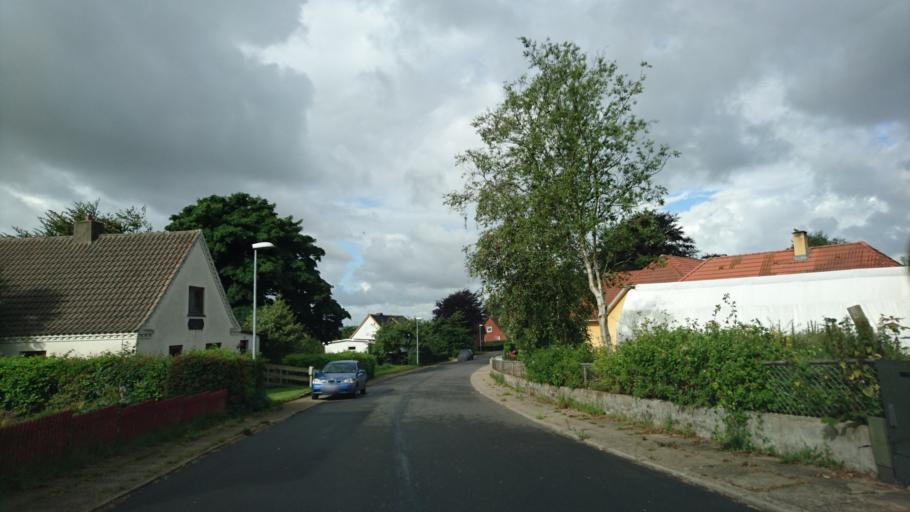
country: DK
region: North Denmark
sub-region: Hjorring Kommune
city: Sindal
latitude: 57.3776
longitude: 10.2240
